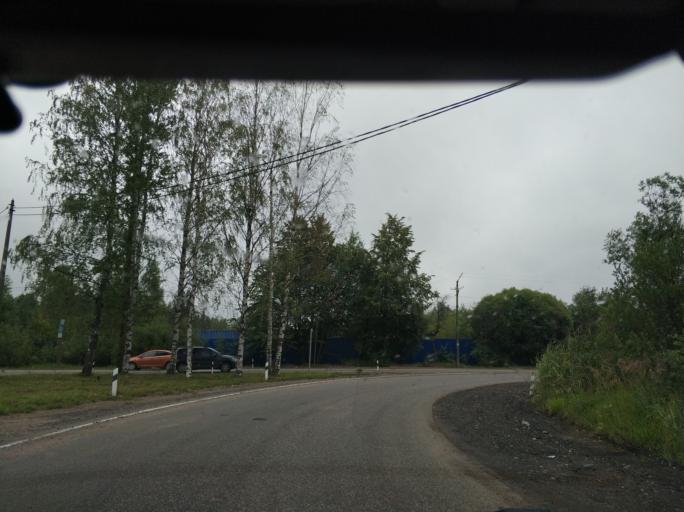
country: RU
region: Leningrad
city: Imeni Morozova
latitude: 59.9760
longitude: 31.0243
